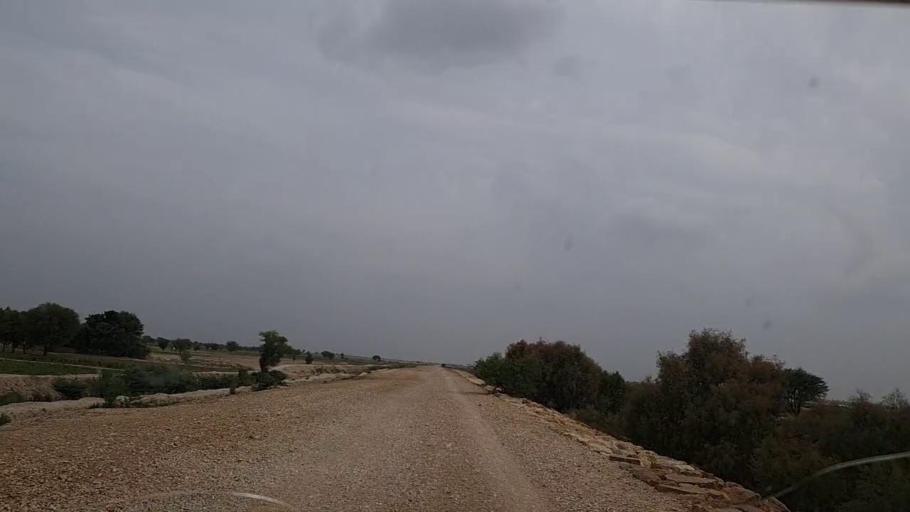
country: PK
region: Sindh
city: Johi
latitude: 26.7164
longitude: 67.5818
